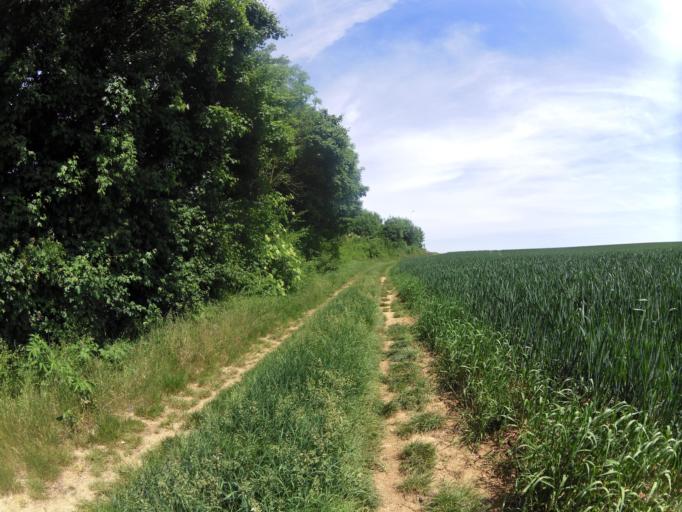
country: DE
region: Bavaria
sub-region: Regierungsbezirk Unterfranken
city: Sommerhausen
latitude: 49.6712
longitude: 10.0215
